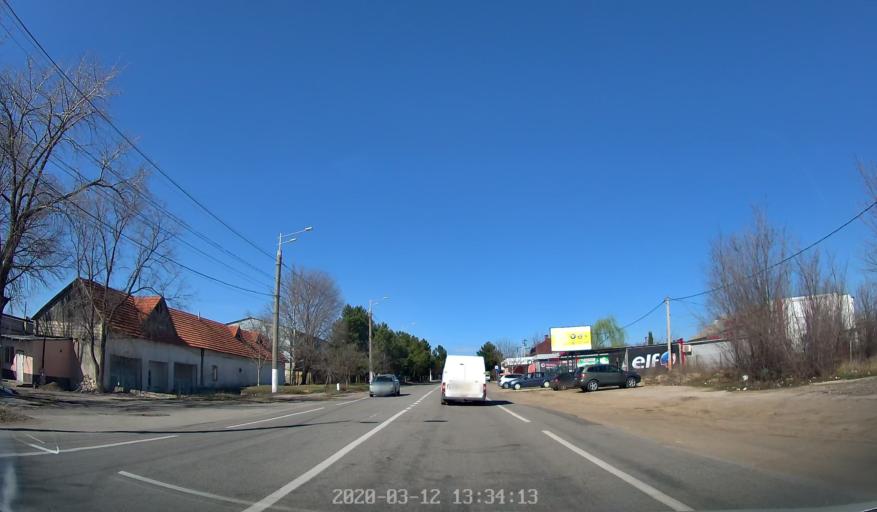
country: MD
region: Laloveni
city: Ialoveni
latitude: 46.9619
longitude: 28.7675
